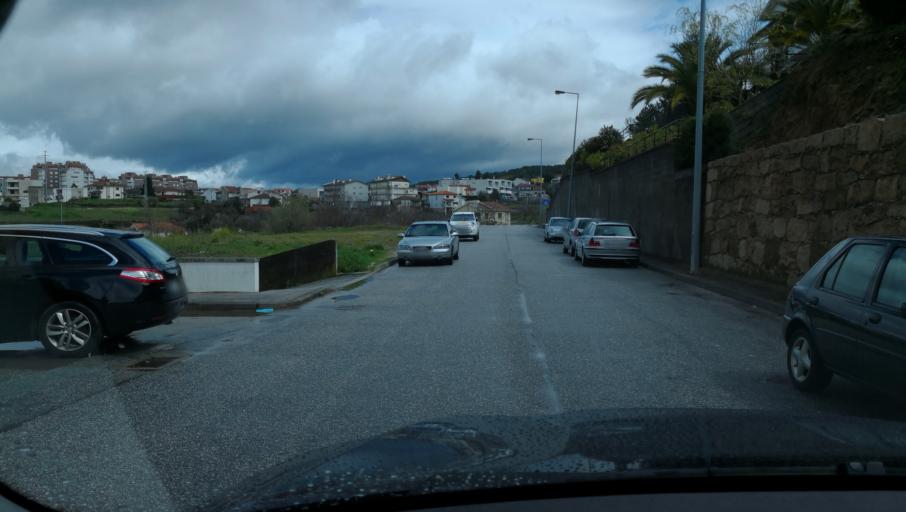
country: PT
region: Vila Real
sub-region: Vila Real
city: Vila Real
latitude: 41.3006
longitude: -7.7227
